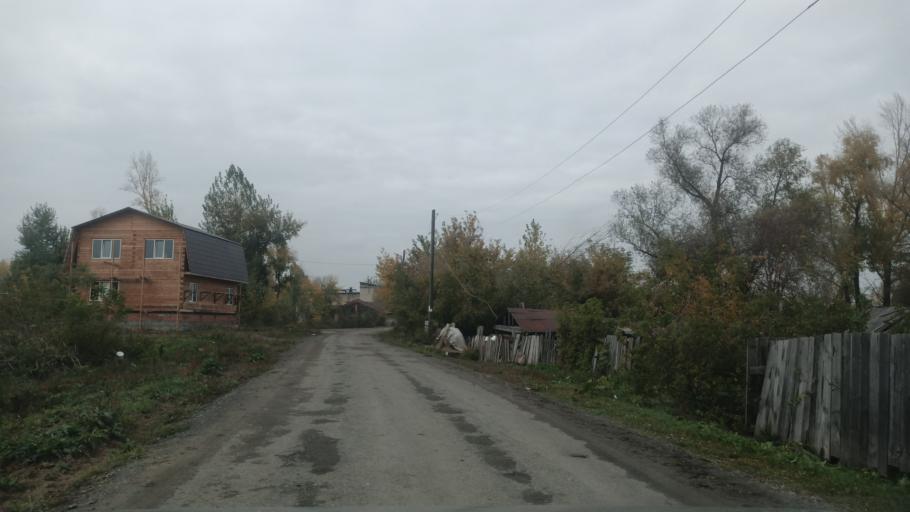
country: RU
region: Altai Krai
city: Zaton
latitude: 53.2983
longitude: 83.8040
